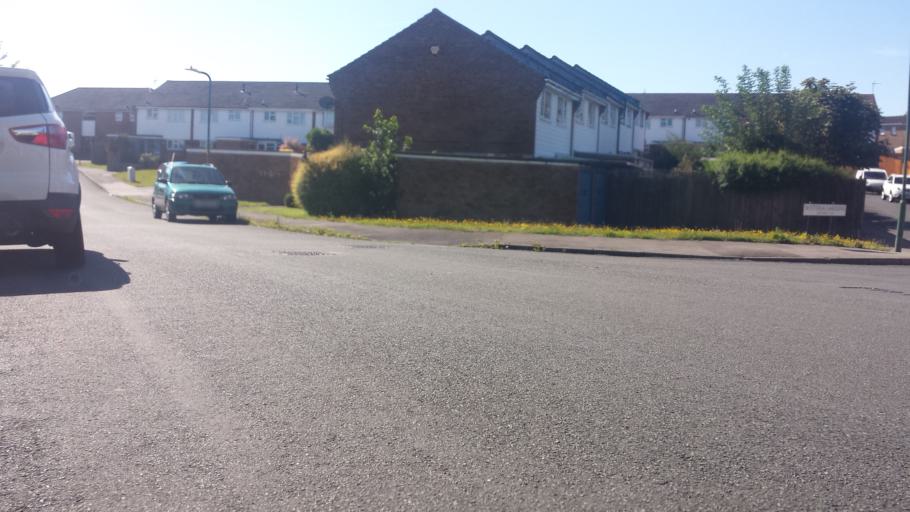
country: GB
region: England
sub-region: Kent
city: Swanley
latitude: 51.4041
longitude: 0.1644
